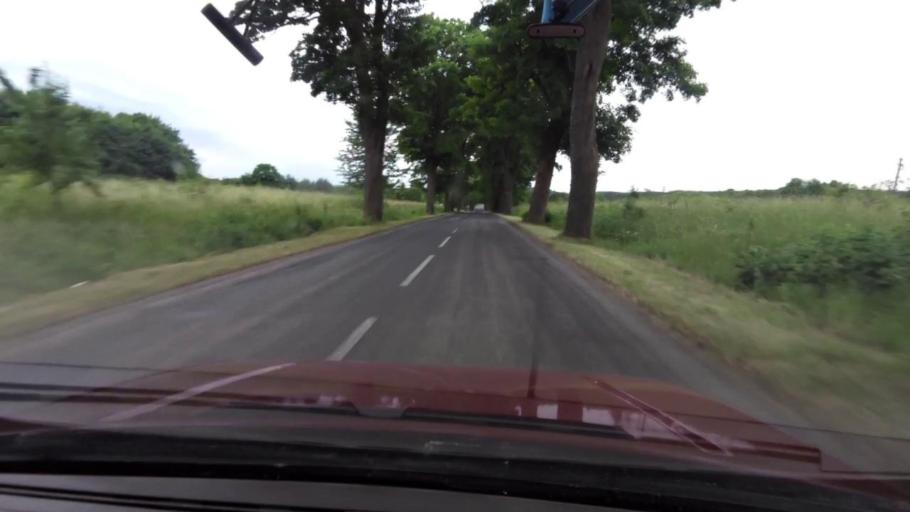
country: PL
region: West Pomeranian Voivodeship
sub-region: Powiat koszalinski
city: Sianow
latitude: 54.1751
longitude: 16.3912
